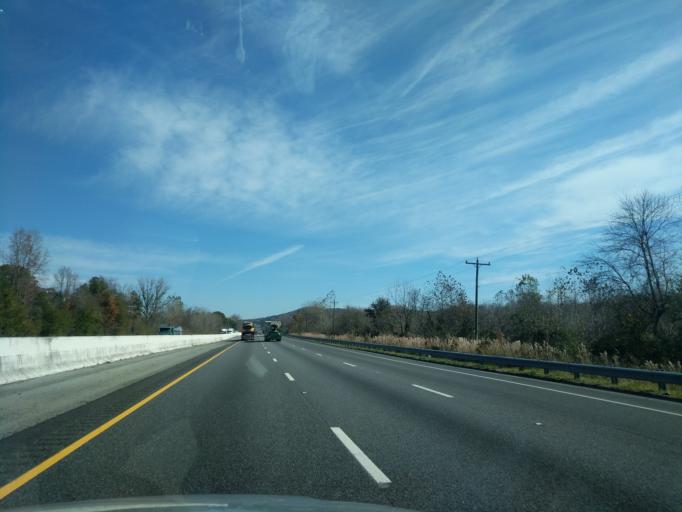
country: US
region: South Carolina
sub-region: Cherokee County
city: Blacksburg
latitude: 35.1292
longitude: -81.5498
